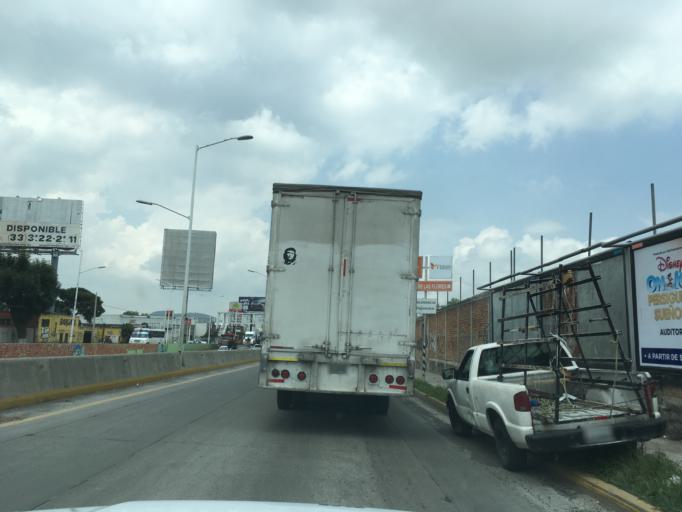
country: MX
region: Jalisco
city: Nicolas R Casillas
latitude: 20.5582
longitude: -103.4643
